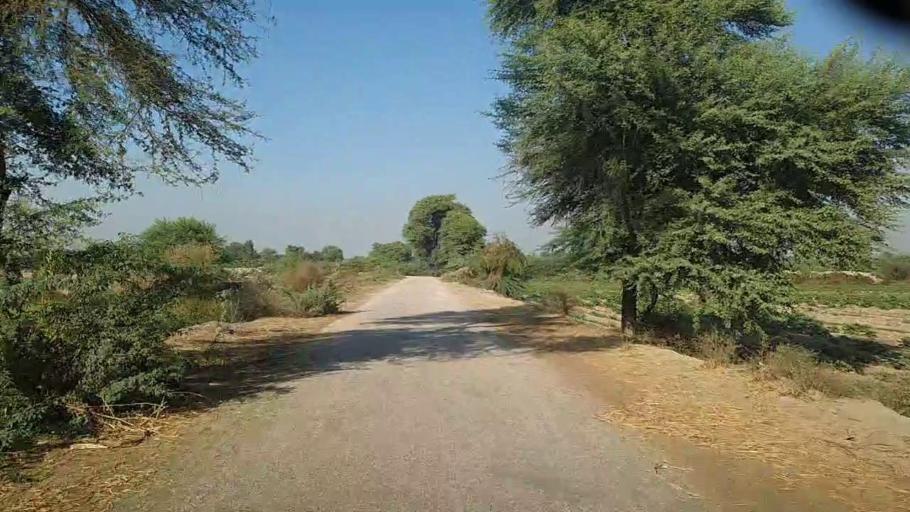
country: PK
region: Sindh
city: Darya Khan Marri
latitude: 26.6884
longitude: 68.3515
